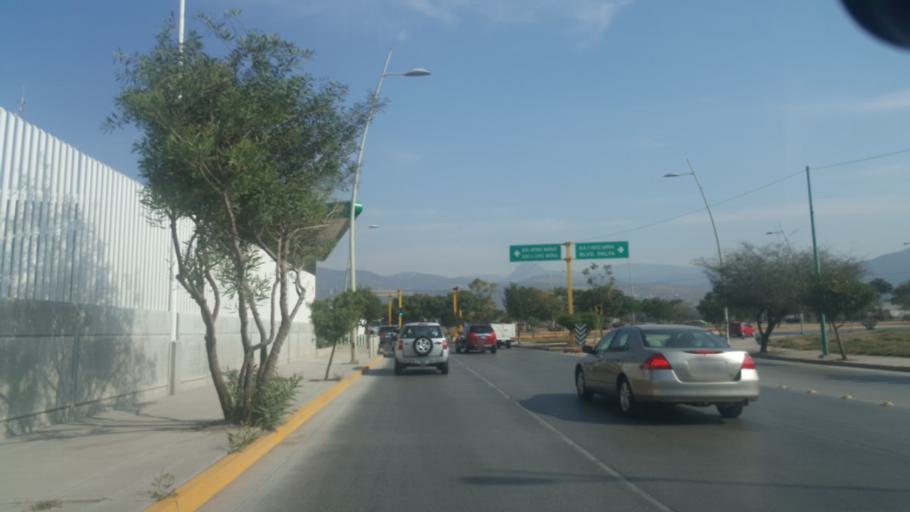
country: MX
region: Guanajuato
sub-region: Leon
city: Medina
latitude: 21.1397
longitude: -101.6315
